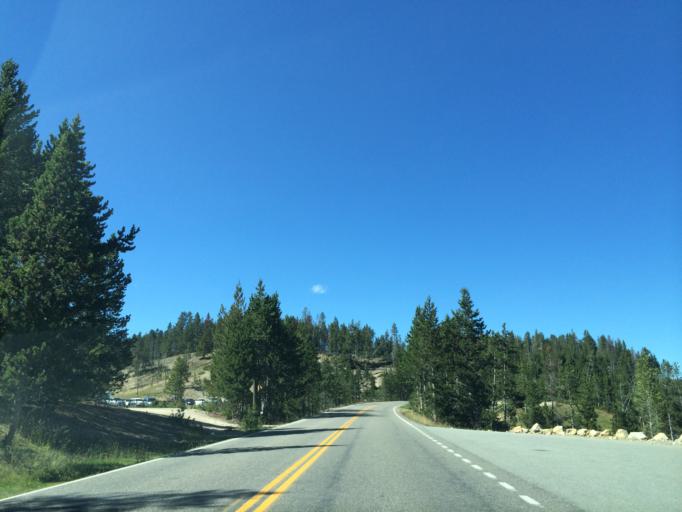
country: US
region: Montana
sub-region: Gallatin County
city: West Yellowstone
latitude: 44.6243
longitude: -110.4321
